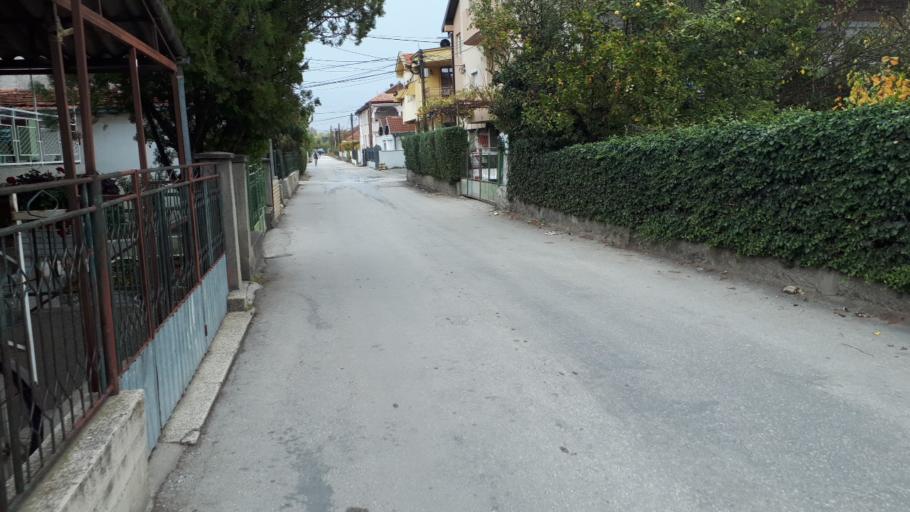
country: MK
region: Saraj
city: Saraj
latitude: 42.0195
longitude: 21.3560
